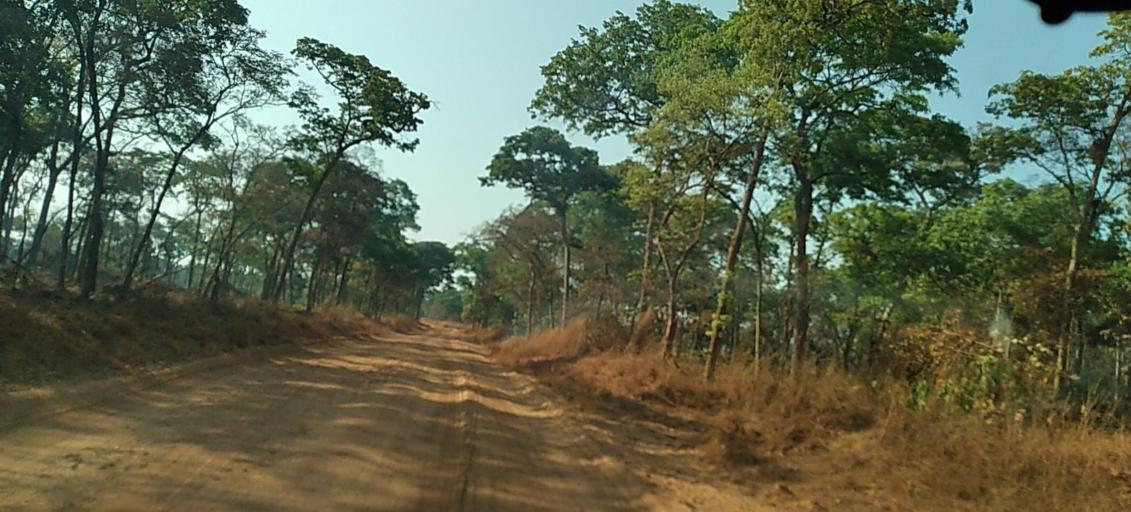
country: ZM
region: North-Western
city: Kasempa
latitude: -13.6471
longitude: 26.0014
